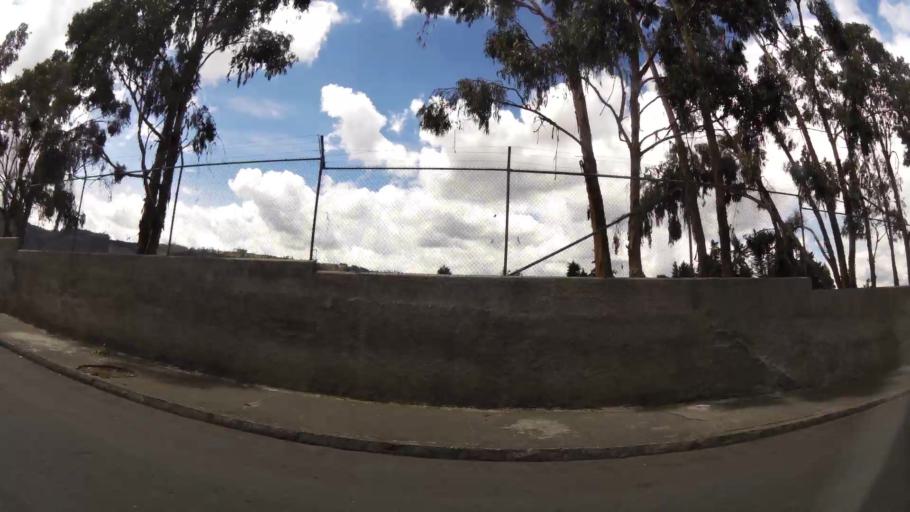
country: EC
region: Tungurahua
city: Ambato
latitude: -1.2539
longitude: -78.6358
